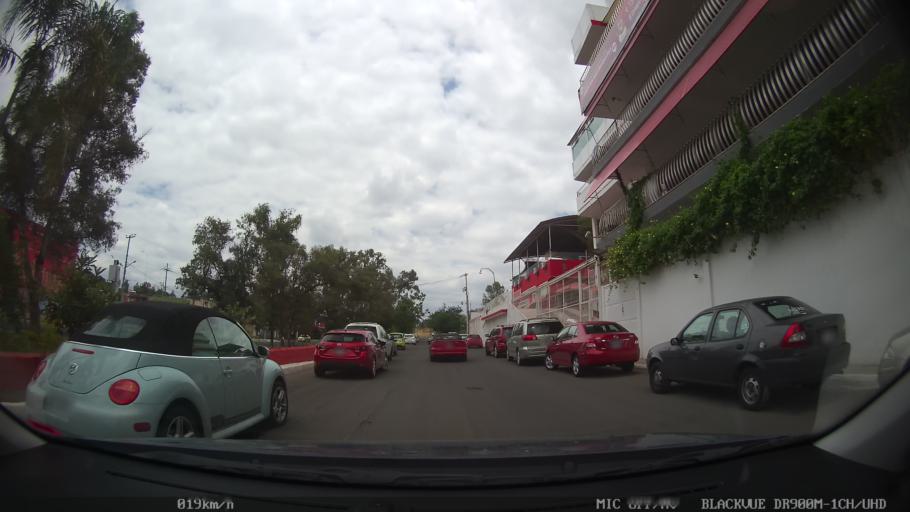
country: MX
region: Jalisco
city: Tlaquepaque
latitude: 20.6417
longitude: -103.2802
